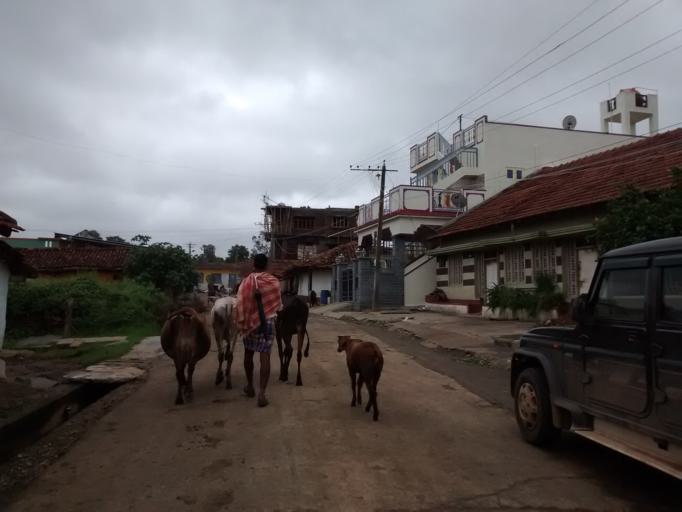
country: IN
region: Karnataka
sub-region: Hassan
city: Hassan
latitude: 12.9290
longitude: 76.1855
